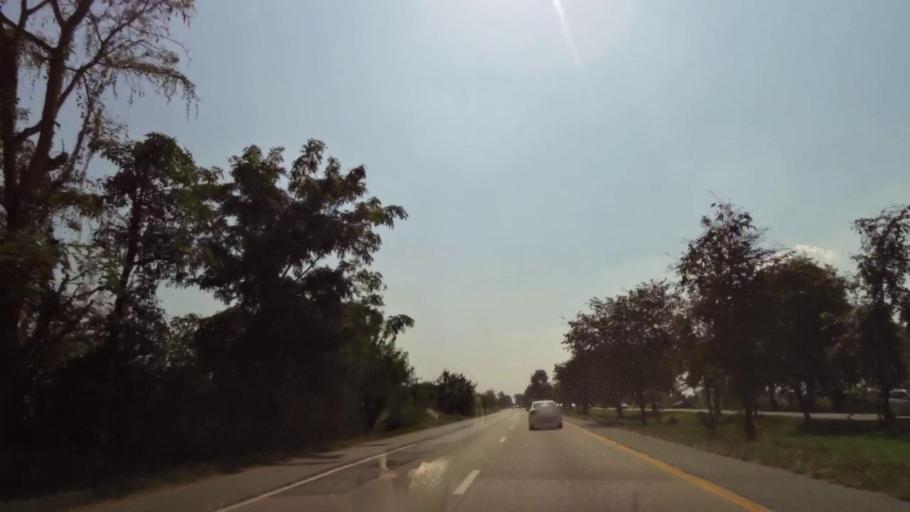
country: TH
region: Phichit
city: Wachira Barami
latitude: 16.5875
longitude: 100.1471
